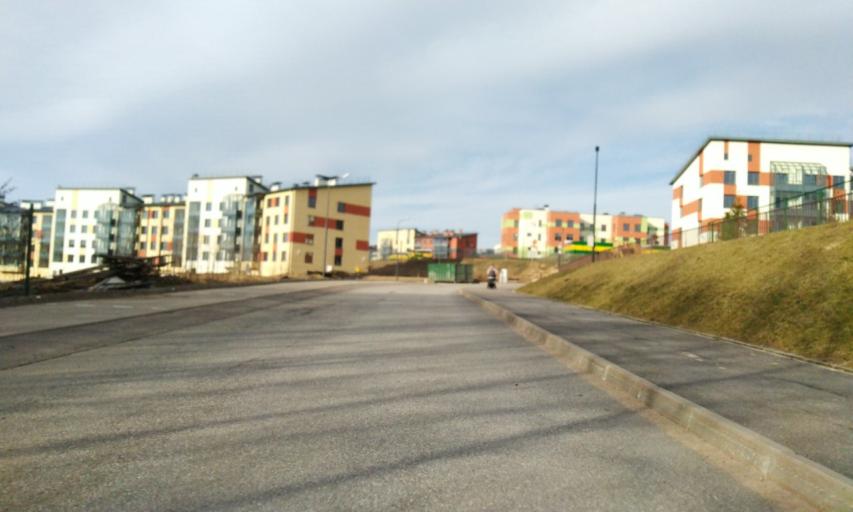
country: RU
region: Leningrad
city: Bugry
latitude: 60.1206
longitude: 30.4214
